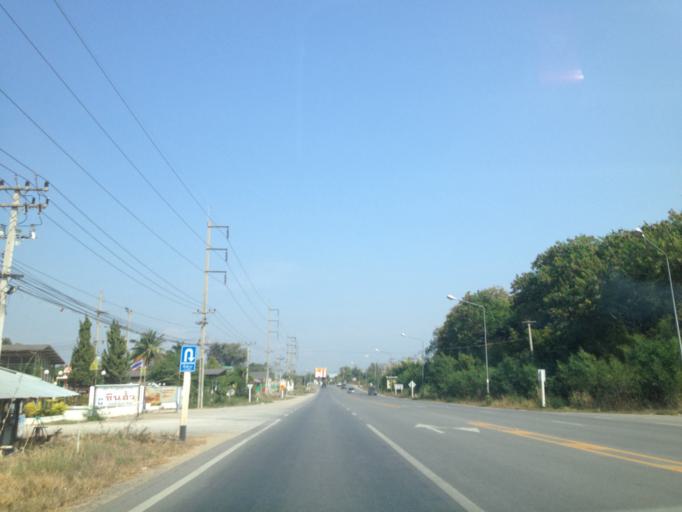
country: TH
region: Chiang Mai
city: Chom Thong
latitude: 18.3413
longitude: 98.6783
